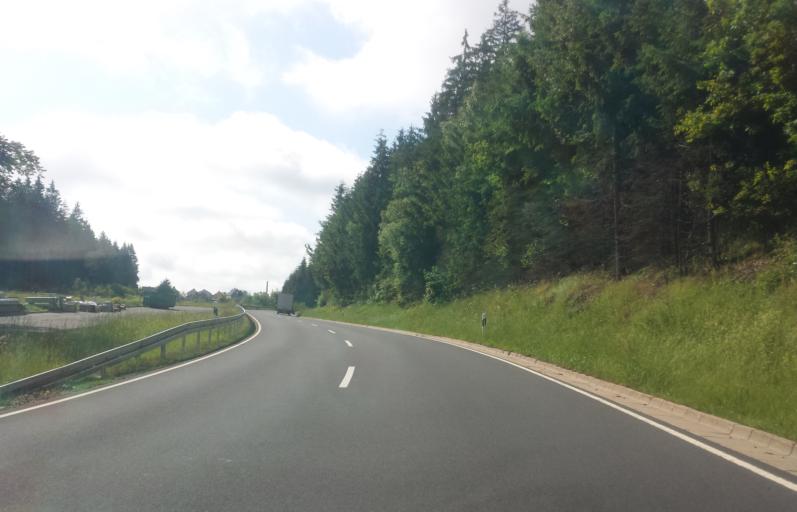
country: DE
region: Bavaria
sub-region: Upper Franconia
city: Ludwigsstadt
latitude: 50.4488
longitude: 11.3726
